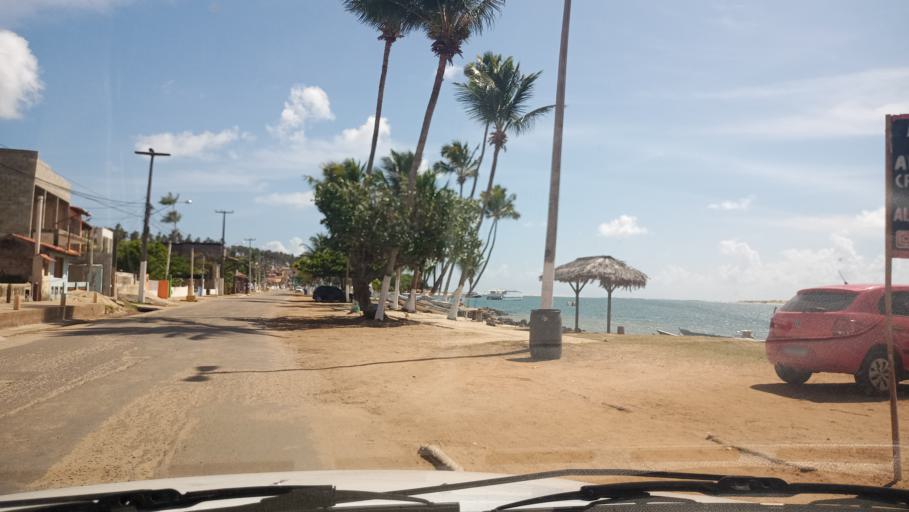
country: BR
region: Rio Grande do Norte
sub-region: Canguaretama
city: Canguaretama
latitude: -6.3179
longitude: -35.0460
